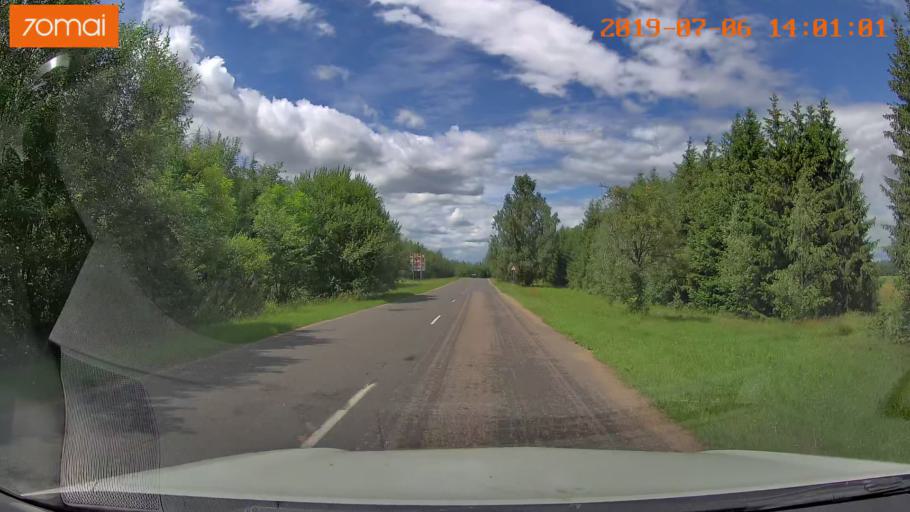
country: BY
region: Minsk
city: Ivyanyets
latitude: 53.8039
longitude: 26.8169
